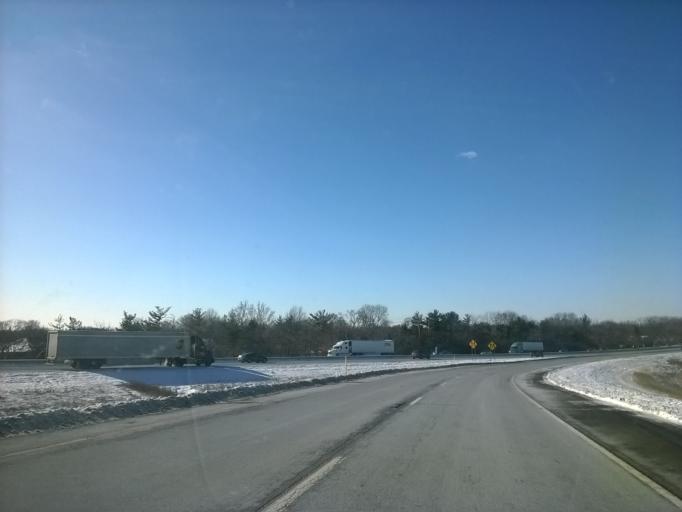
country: US
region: Indiana
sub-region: Marion County
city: Lawrence
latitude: 39.8981
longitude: -86.0576
